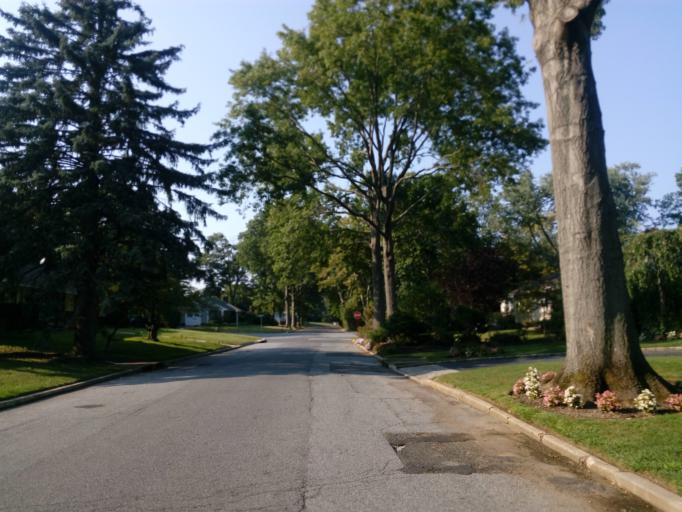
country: US
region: New York
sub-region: Nassau County
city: Locust Valley
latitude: 40.8595
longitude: -73.6027
